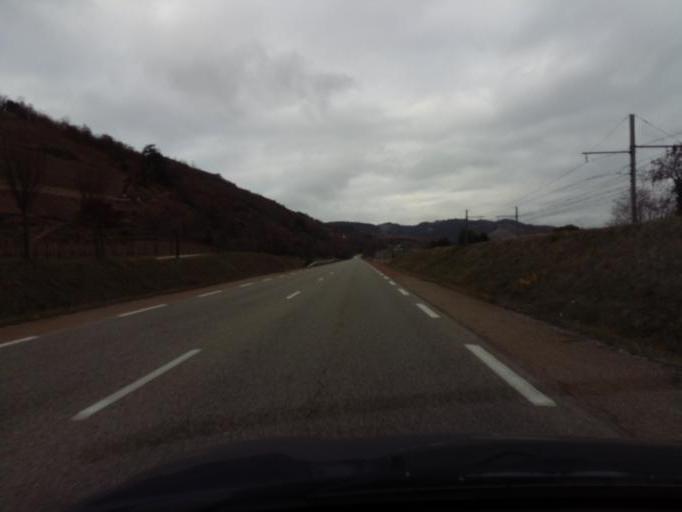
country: FR
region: Rhone-Alpes
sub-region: Departement de l'Ardeche
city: Mauves
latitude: 45.0284
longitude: 4.8297
